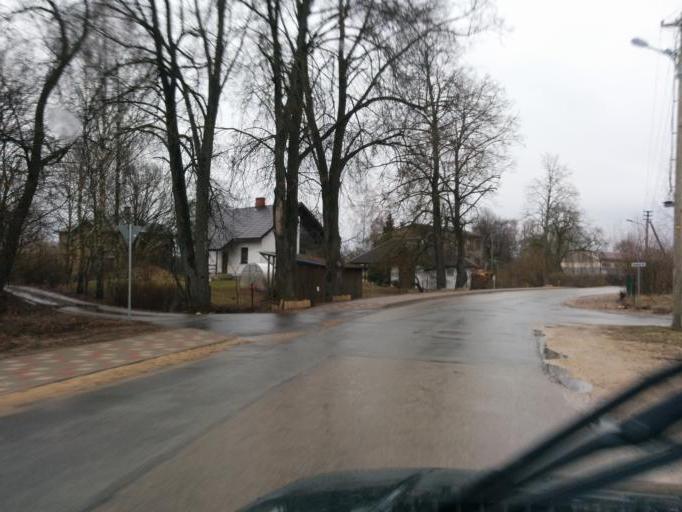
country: LV
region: Kekava
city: Kekava
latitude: 56.8723
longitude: 24.1854
